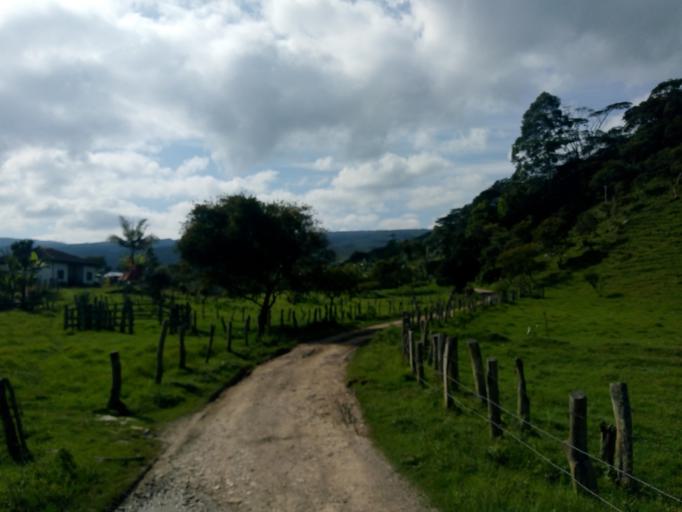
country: CO
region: Boyaca
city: Moniquira
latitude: 5.8758
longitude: -73.5056
